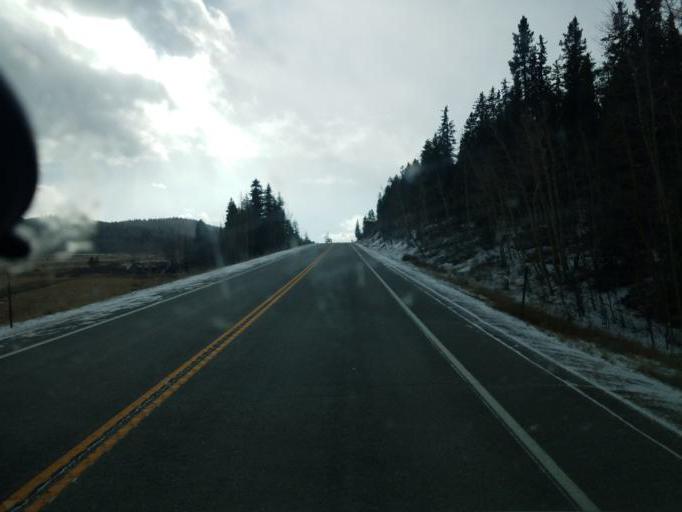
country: US
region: Colorado
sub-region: Summit County
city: Breckenridge
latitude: 39.4159
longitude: -105.7613
